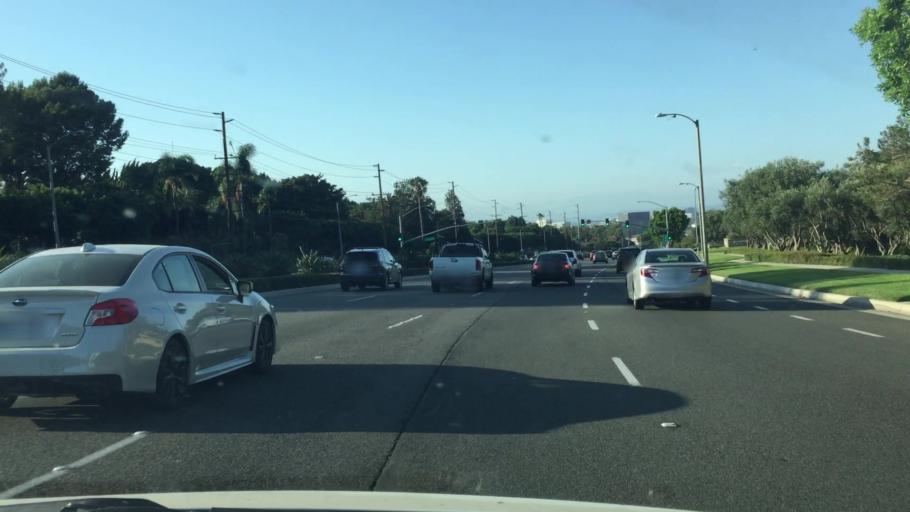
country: US
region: California
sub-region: Orange County
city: San Joaquin Hills
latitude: 33.6324
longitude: -117.8630
